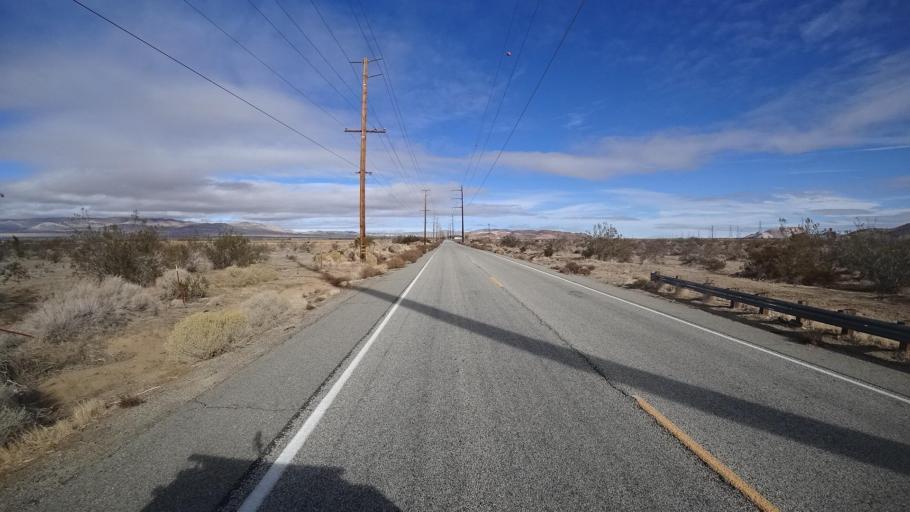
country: US
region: California
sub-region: Kern County
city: Rosamond
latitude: 34.9057
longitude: -118.2913
